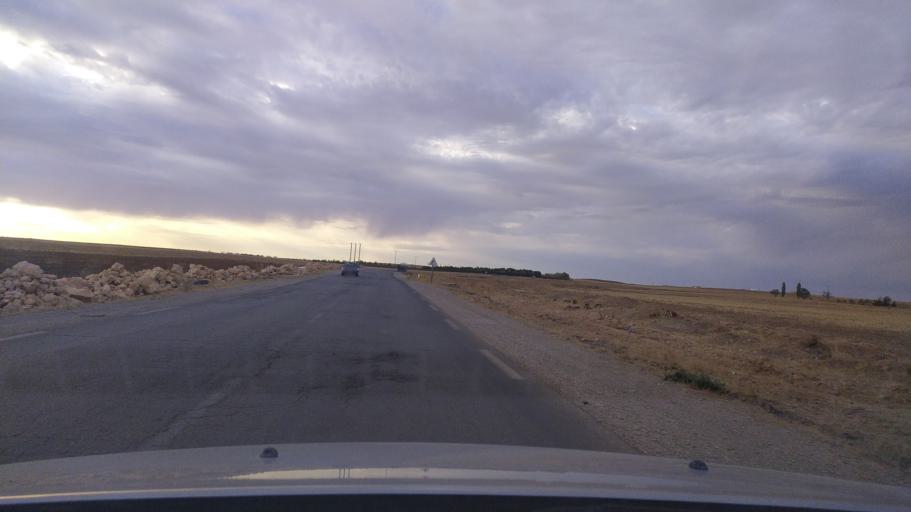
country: DZ
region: Tiaret
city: Frenda
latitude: 34.9812
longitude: 1.1468
